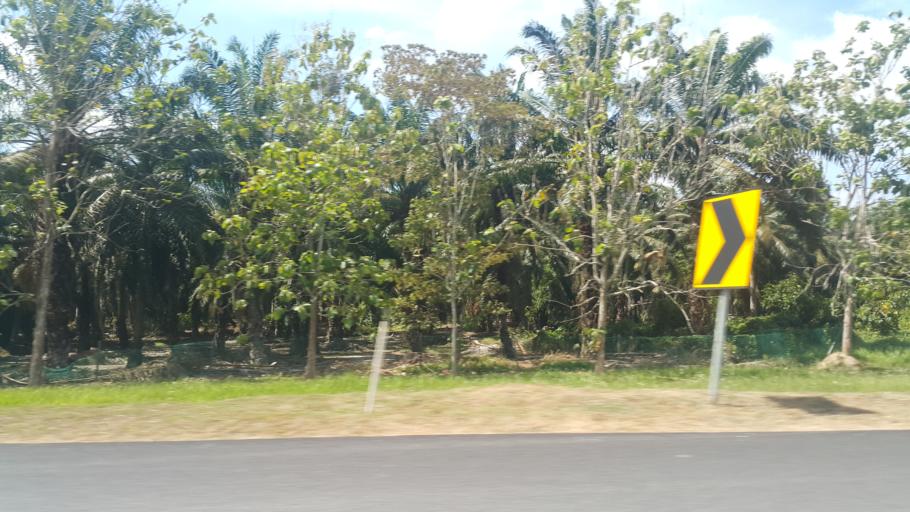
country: MY
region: Johor
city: Bakri
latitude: 2.1553
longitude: 102.6640
